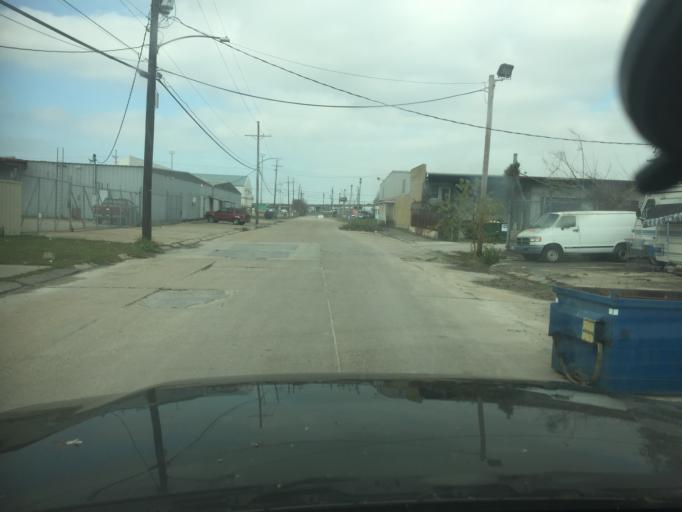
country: US
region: Louisiana
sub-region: Saint Bernard Parish
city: Arabi
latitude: 29.9975
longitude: -90.0325
